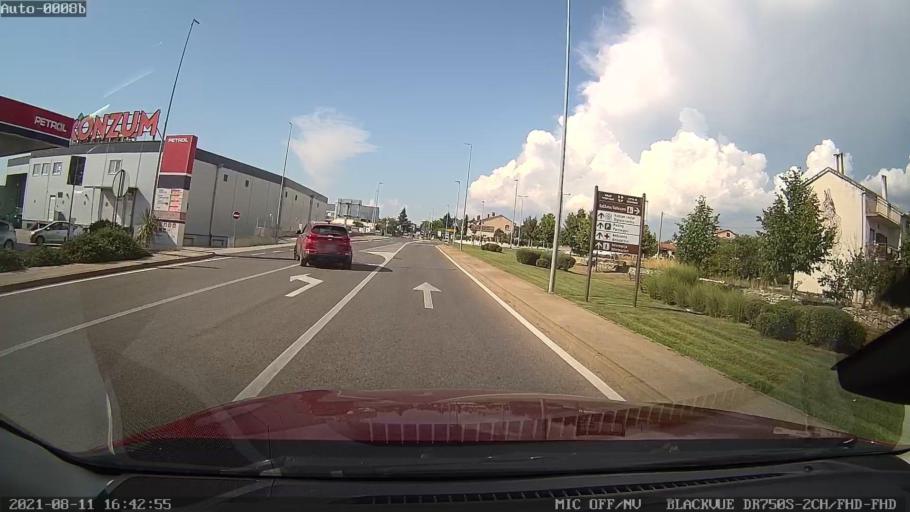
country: HR
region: Istarska
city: Vodnjan
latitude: 44.9532
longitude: 13.8538
